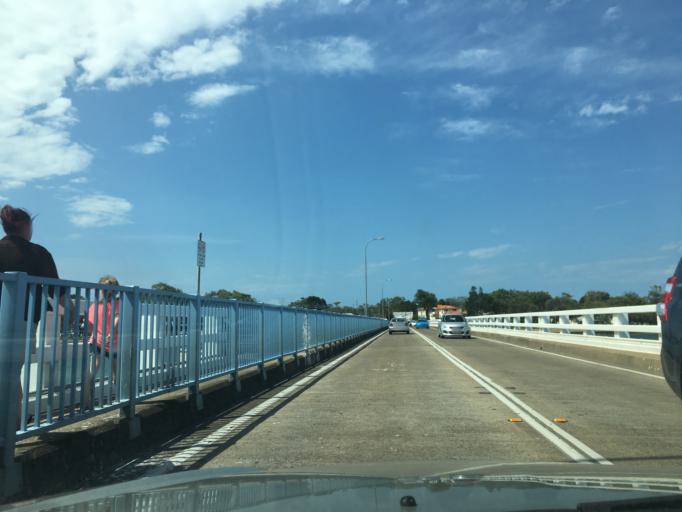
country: AU
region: Queensland
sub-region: Moreton Bay
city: Bongaree
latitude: -27.0697
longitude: 153.1465
